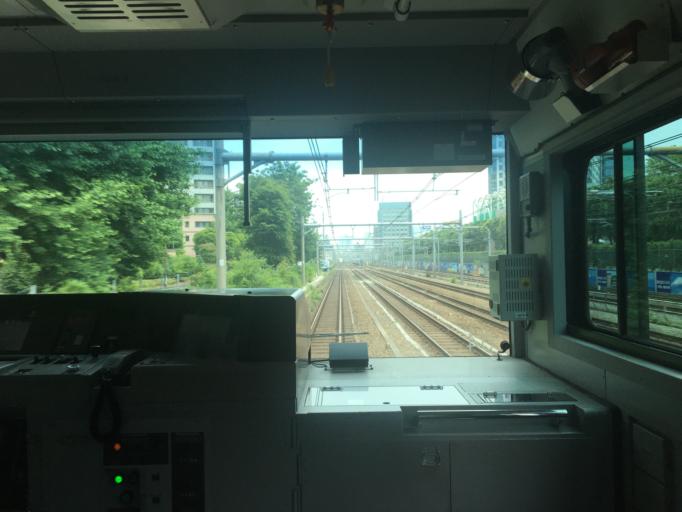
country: JP
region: Tokyo
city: Tokyo
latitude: 35.7054
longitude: 139.7011
